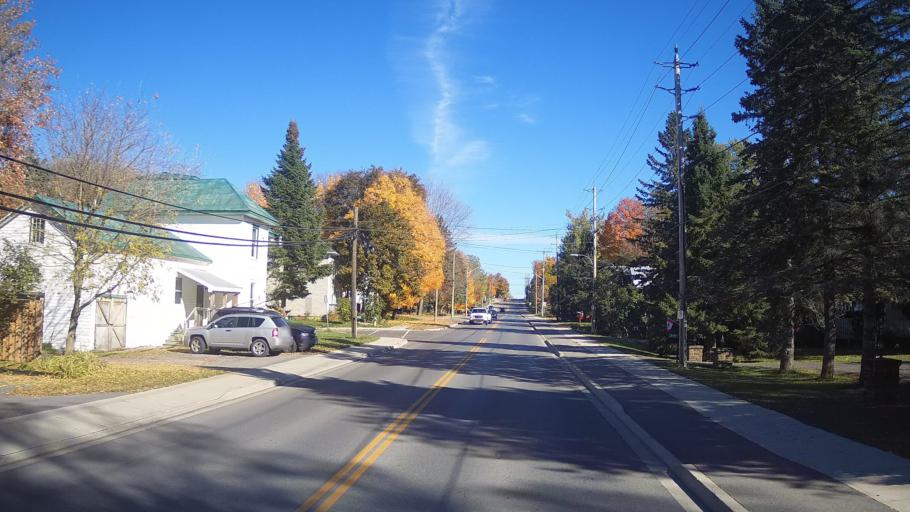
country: CA
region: Ontario
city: Kingston
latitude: 44.4068
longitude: -76.6011
